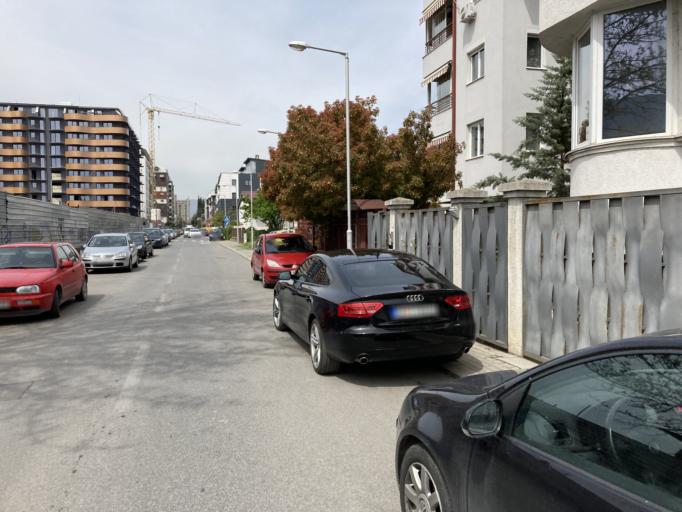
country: MK
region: Karpos
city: Skopje
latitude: 41.9980
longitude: 21.4015
